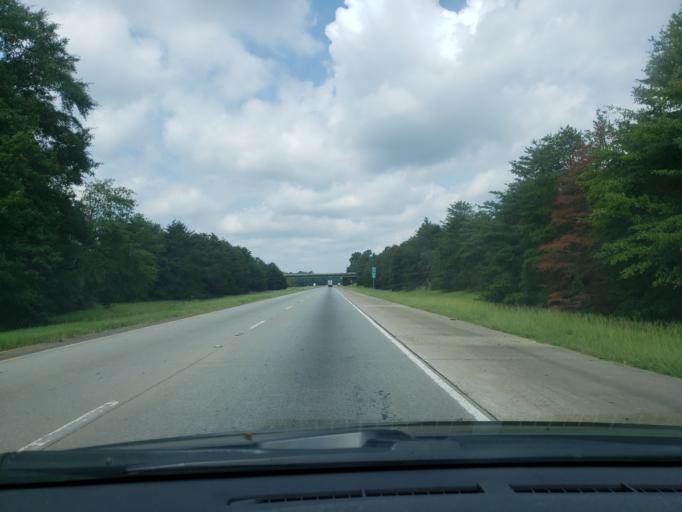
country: US
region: Georgia
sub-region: Treutlen County
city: Soperton
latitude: 32.4235
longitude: -82.4294
